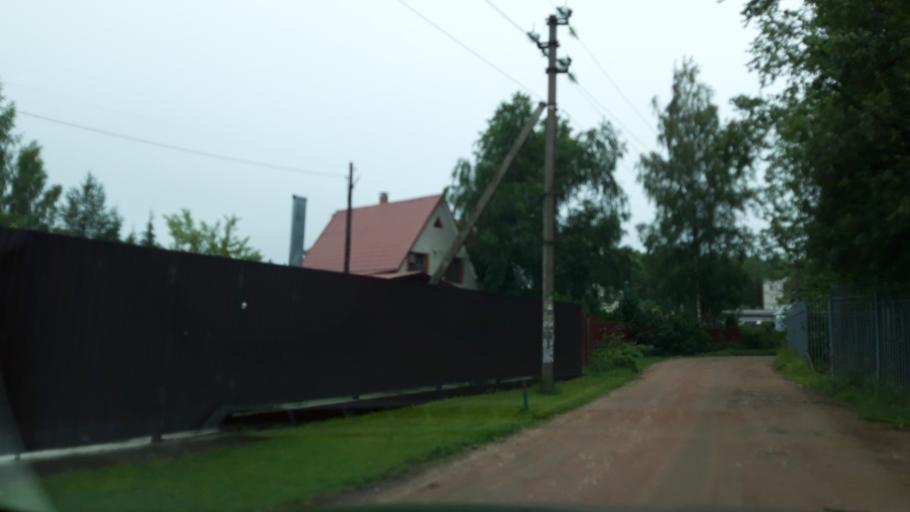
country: RU
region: Tverskaya
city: Konakovo
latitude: 56.6580
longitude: 36.6558
